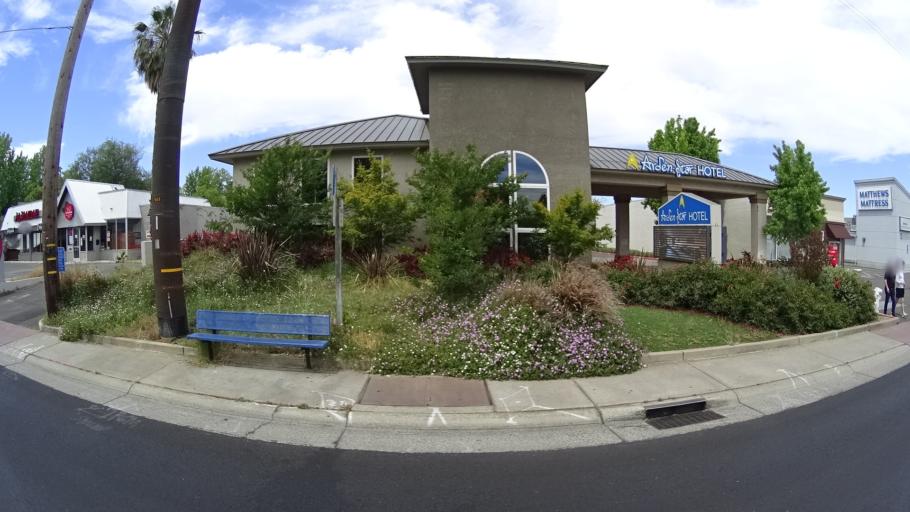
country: US
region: California
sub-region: Sacramento County
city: Arden-Arcade
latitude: 38.5912
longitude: -121.4155
